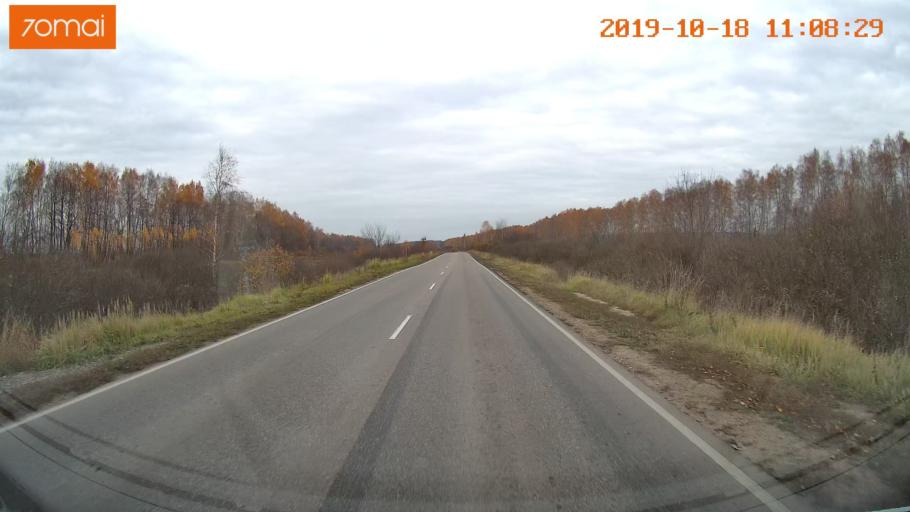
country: RU
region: Tula
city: Kimovsk
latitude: 53.9387
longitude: 38.5370
